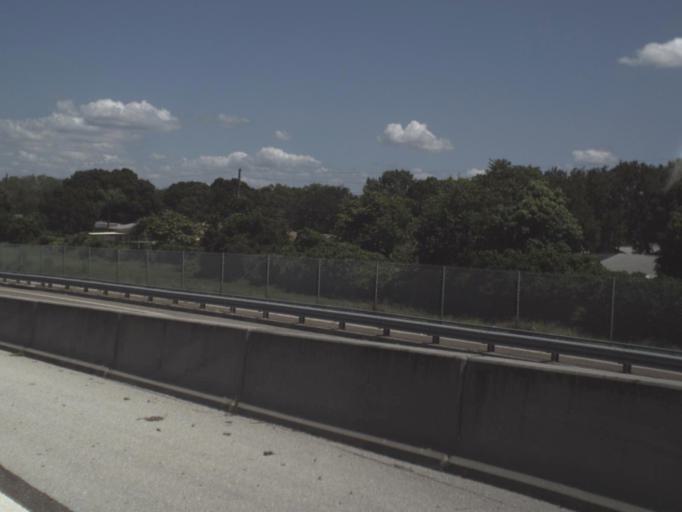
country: US
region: Florida
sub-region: Pinellas County
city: Pinellas Park
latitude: 27.8738
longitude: -82.7266
